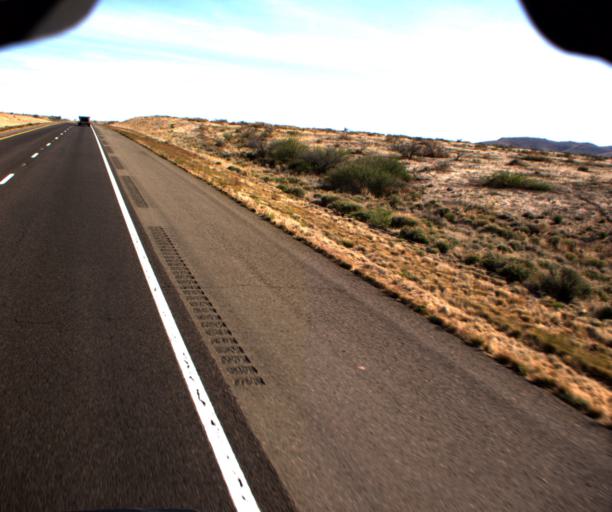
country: US
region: Arizona
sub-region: Cochise County
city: Willcox
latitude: 32.3846
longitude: -109.6666
